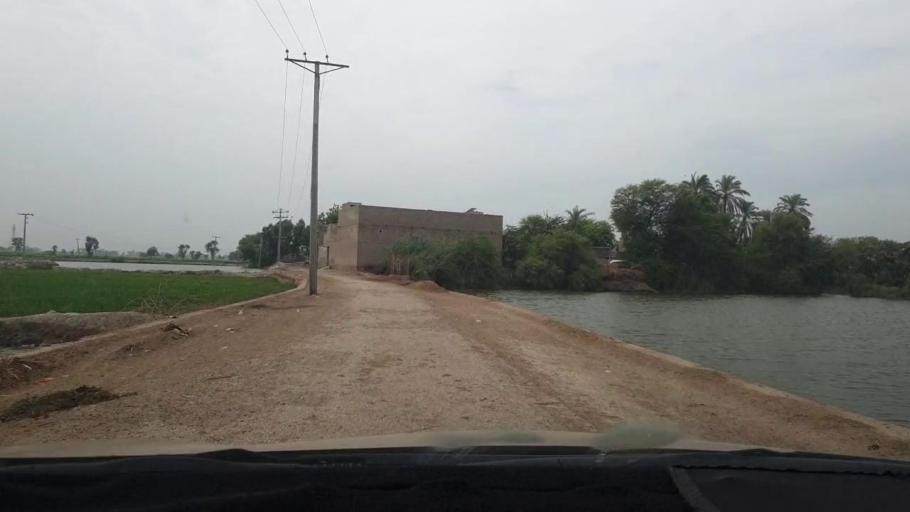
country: PK
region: Sindh
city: Naudero
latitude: 27.6778
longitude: 68.3347
